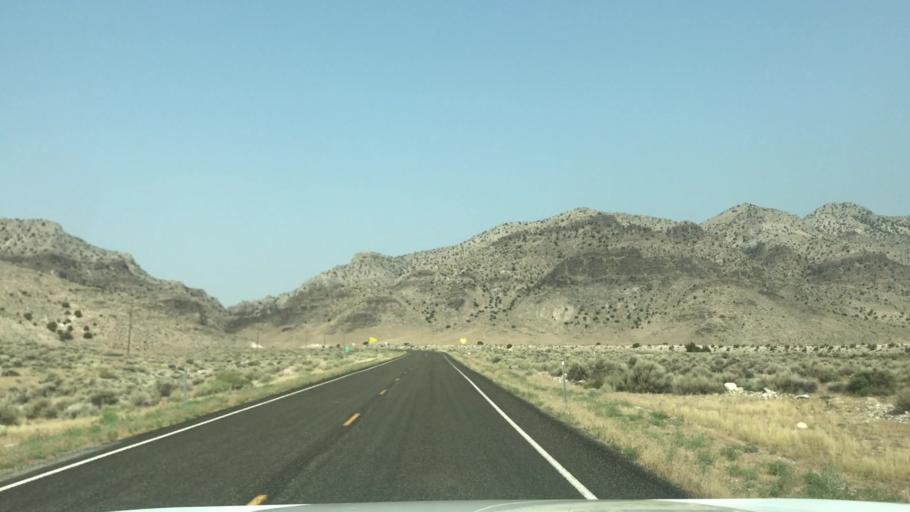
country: US
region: Utah
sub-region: Beaver County
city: Milford
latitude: 39.0881
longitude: -113.5492
